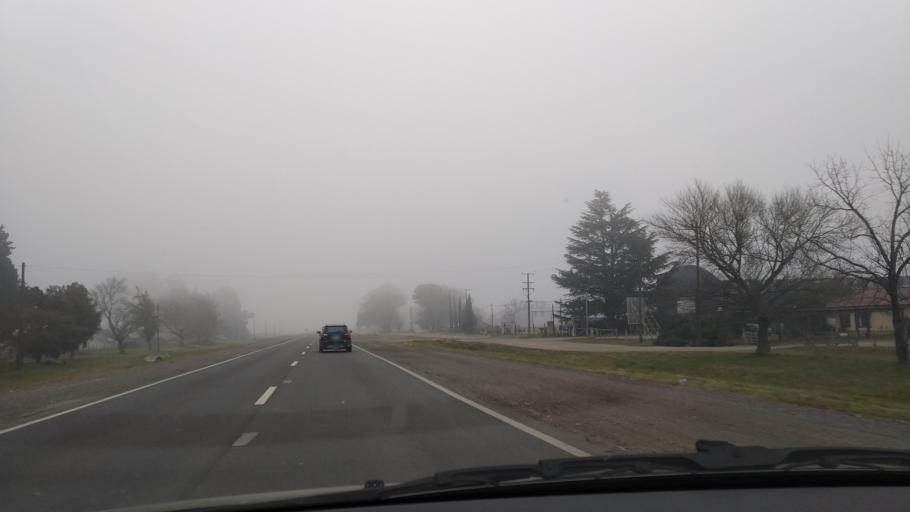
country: AR
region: Buenos Aires
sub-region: Partido de Azul
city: Azul
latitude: -36.8248
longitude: -59.8792
